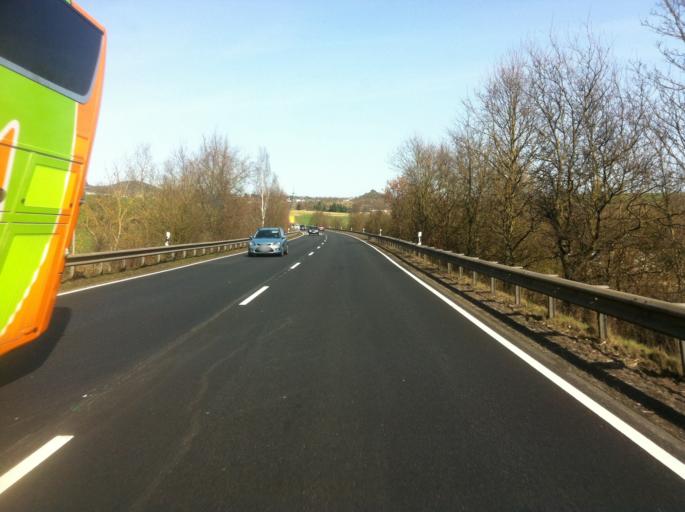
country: DE
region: Rheinland-Pfalz
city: Mayen
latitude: 50.3092
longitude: 7.2395
